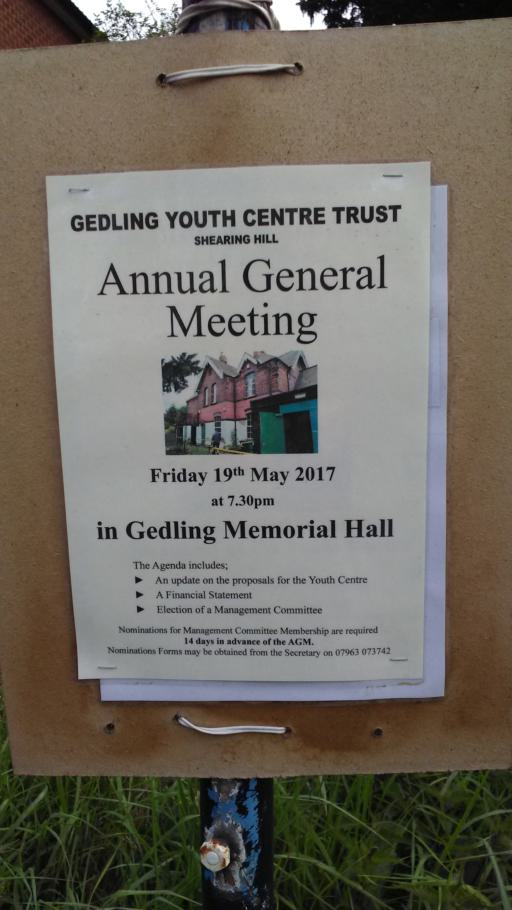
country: GB
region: England
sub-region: Nottinghamshire
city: Burton Joyce
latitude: 52.9747
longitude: -1.0747
